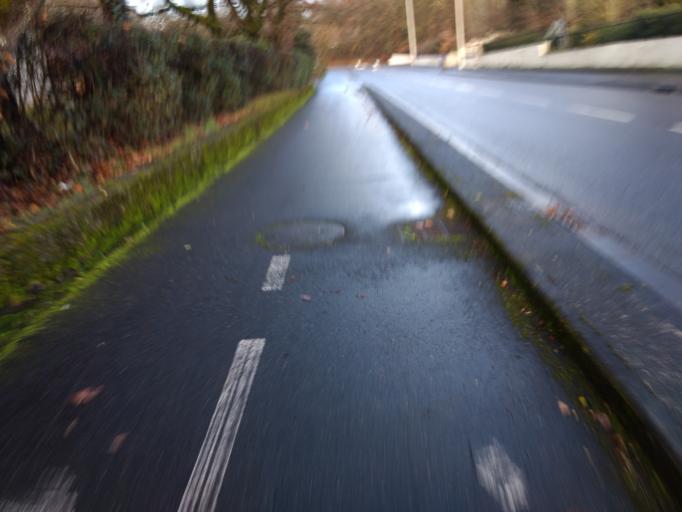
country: FR
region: Midi-Pyrenees
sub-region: Departement de la Haute-Garonne
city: Tournefeuille
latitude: 43.5919
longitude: 1.3387
